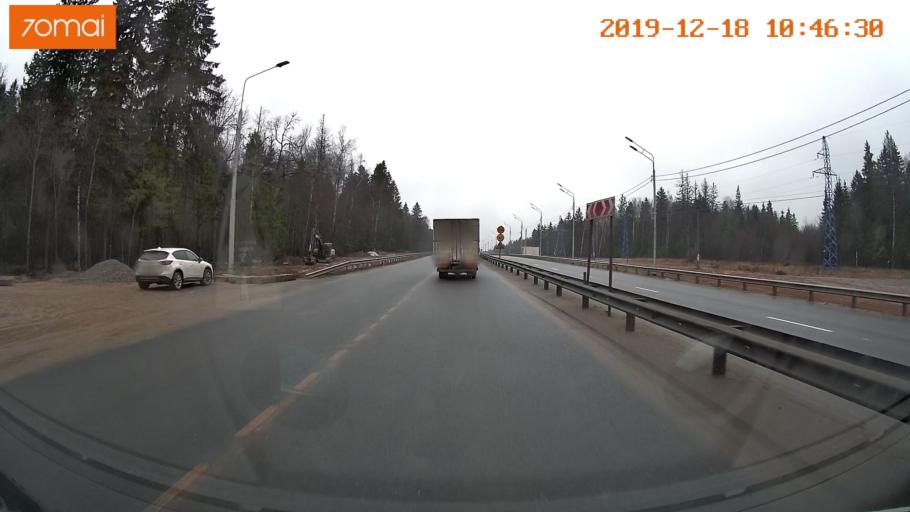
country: RU
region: Moskovskaya
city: Aprelevka
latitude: 55.4846
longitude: 37.0476
